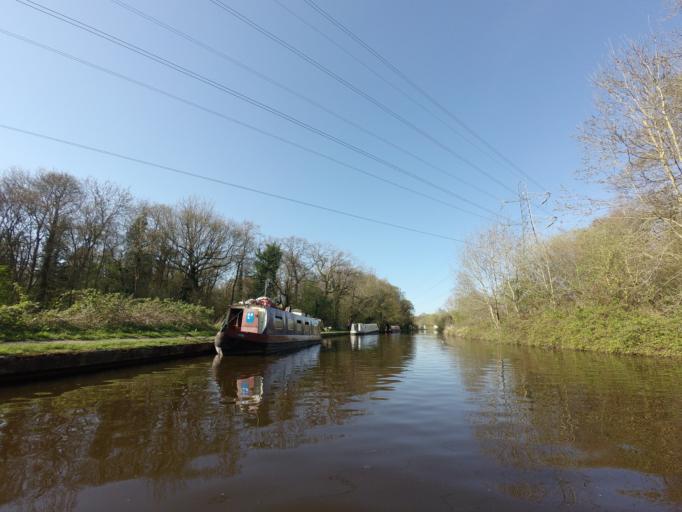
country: GB
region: England
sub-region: Buckinghamshire
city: Denham
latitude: 51.5669
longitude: -0.4825
